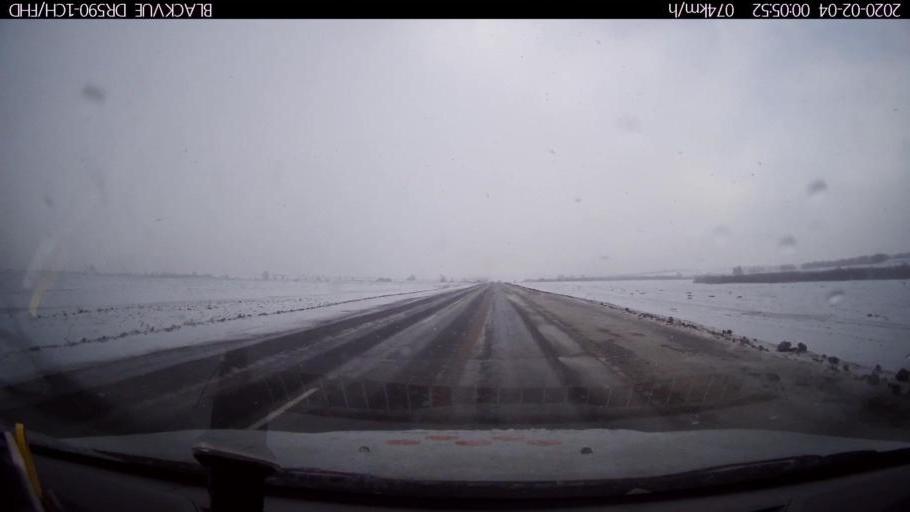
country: RU
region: Nizjnij Novgorod
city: Dal'neye Konstantinovo
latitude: 55.8415
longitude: 44.1263
